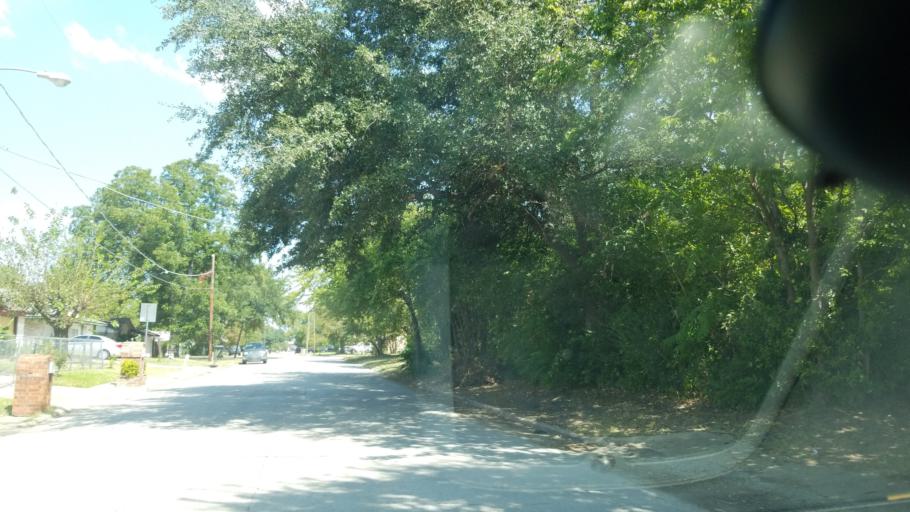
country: US
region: Texas
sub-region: Dallas County
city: Grand Prairie
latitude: 32.7156
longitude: -96.9893
